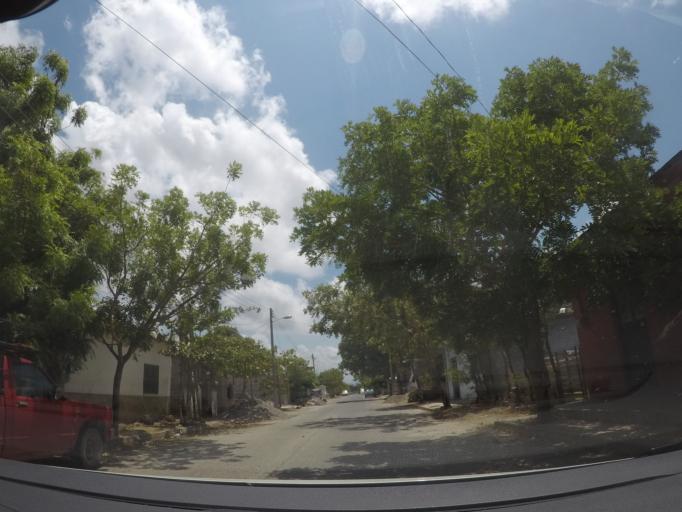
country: MX
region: Oaxaca
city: Juchitan de Zaragoza
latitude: 16.4419
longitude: -95.0117
